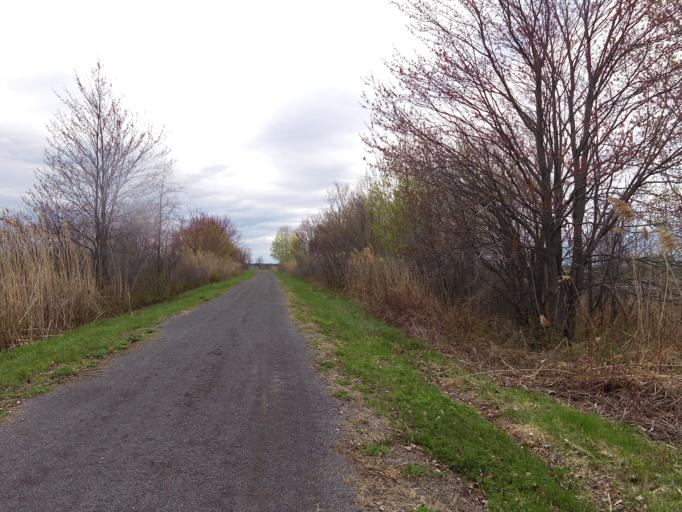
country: CA
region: Ontario
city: Hawkesbury
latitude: 45.5448
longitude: -74.7760
